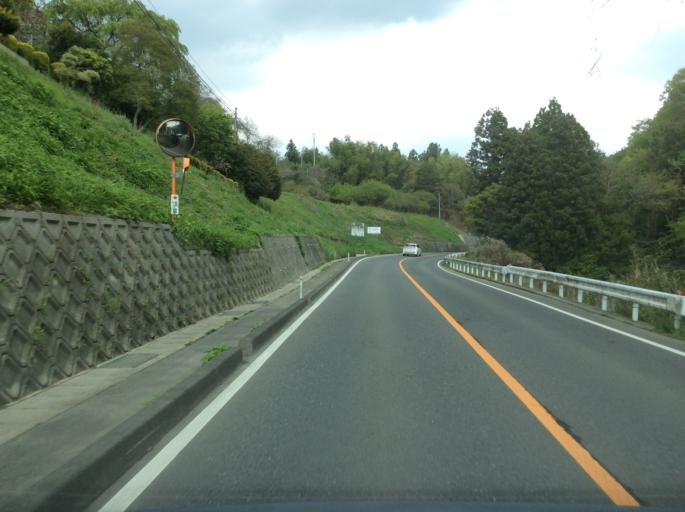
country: JP
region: Fukushima
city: Miharu
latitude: 37.4285
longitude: 140.4582
